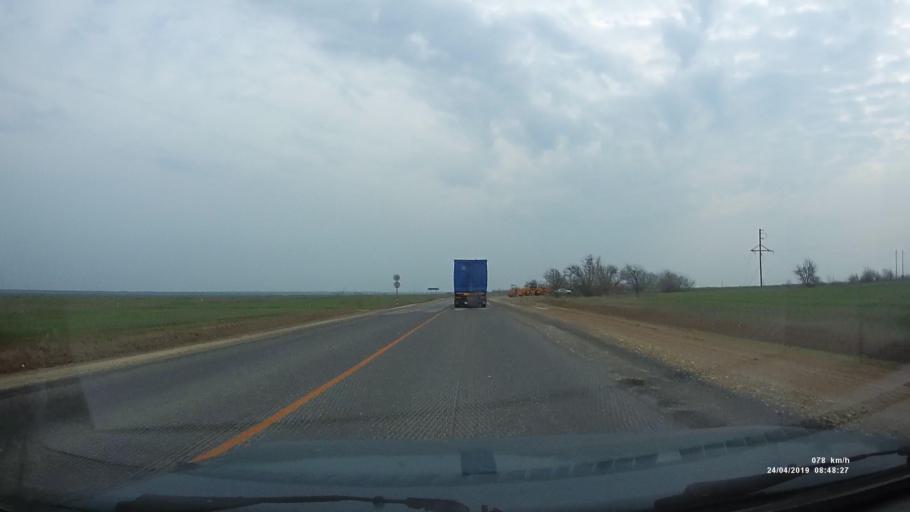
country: RU
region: Kalmykiya
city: Arshan'
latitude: 46.2510
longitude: 44.1089
